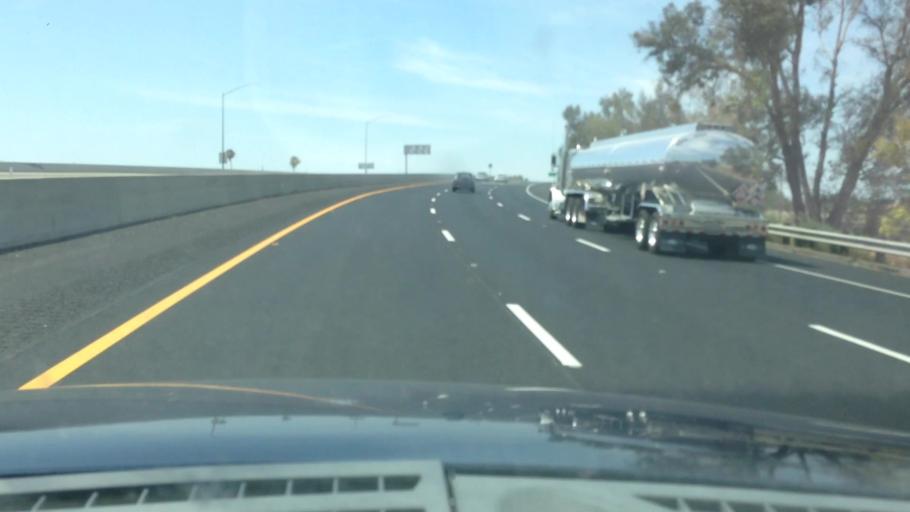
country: US
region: California
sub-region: Kern County
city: Delano
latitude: 35.7874
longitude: -119.2505
